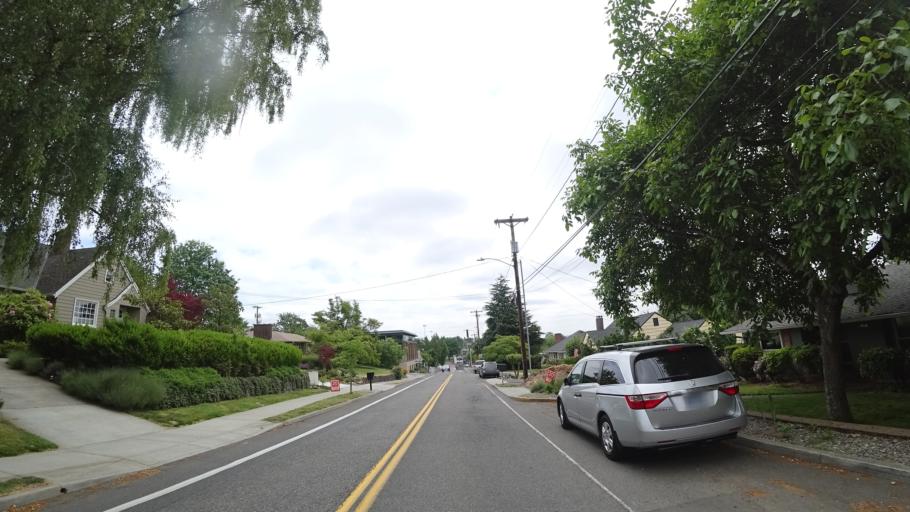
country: US
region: Oregon
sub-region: Multnomah County
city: Portland
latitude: 45.4805
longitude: -122.6952
